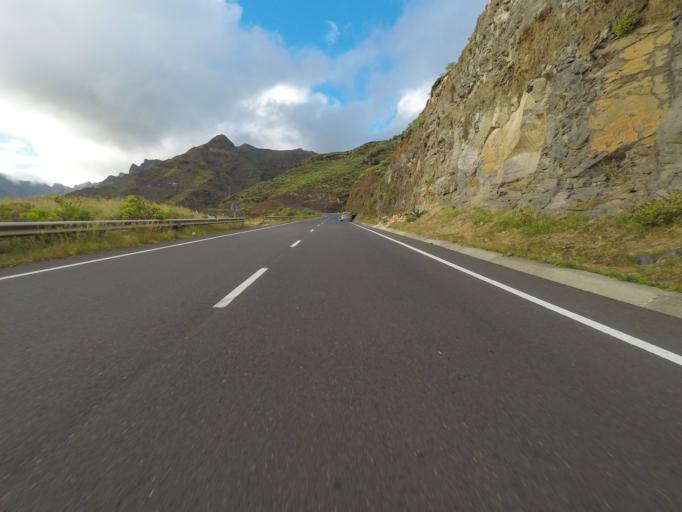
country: ES
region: Canary Islands
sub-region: Provincia de Santa Cruz de Tenerife
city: San Sebastian de la Gomera
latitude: 28.1179
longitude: -17.1419
